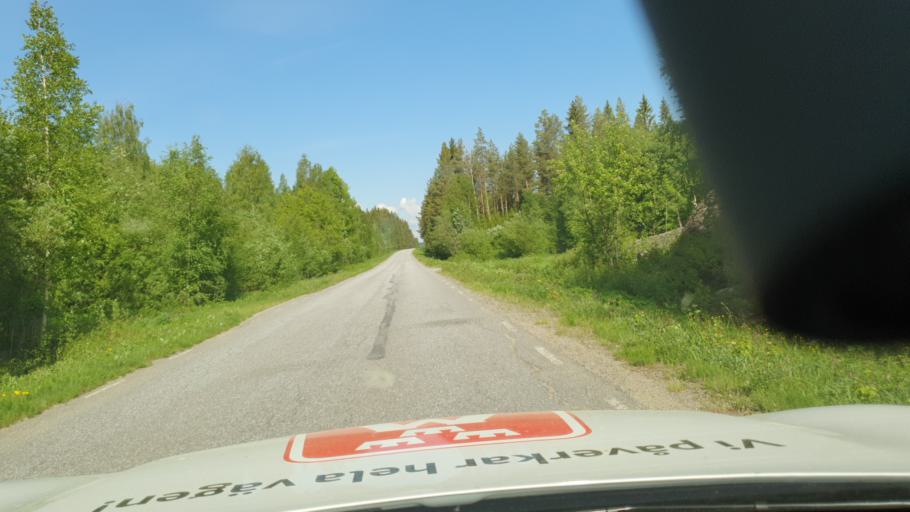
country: SE
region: Vaesterbotten
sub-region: Robertsfors Kommun
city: Robertsfors
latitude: 64.2444
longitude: 20.8480
